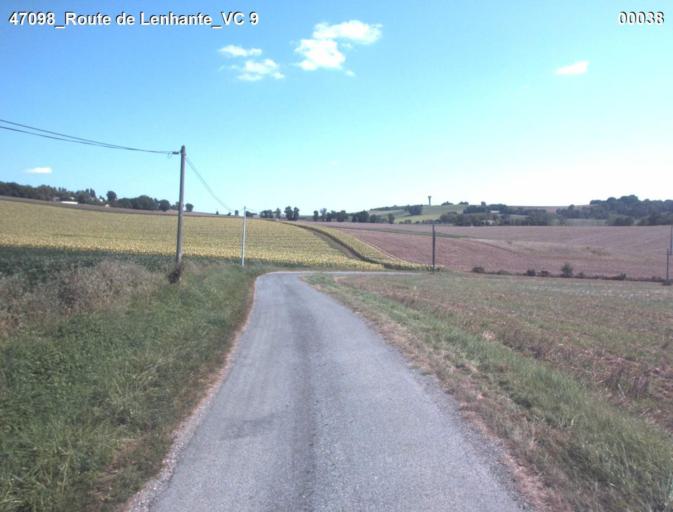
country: FR
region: Aquitaine
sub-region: Departement du Lot-et-Garonne
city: Nerac
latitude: 44.0909
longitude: 0.4157
